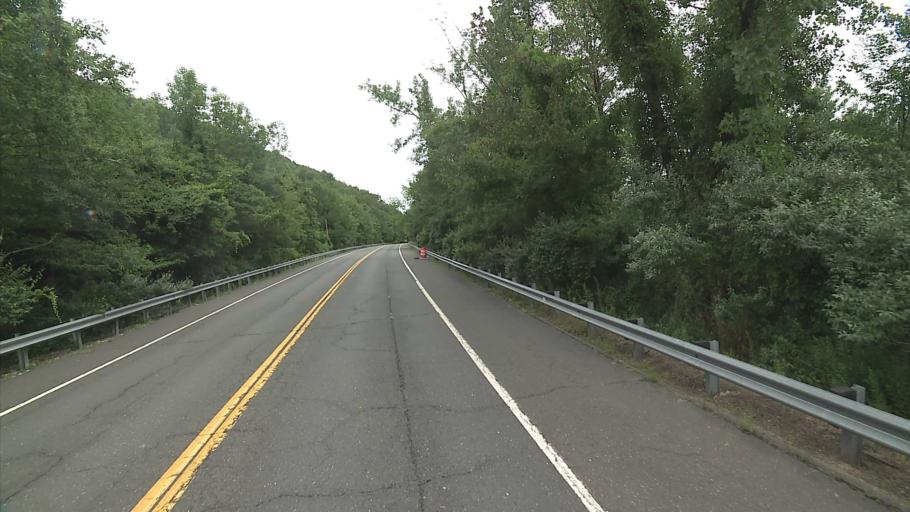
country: US
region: Connecticut
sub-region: Litchfield County
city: Winsted
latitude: 41.9986
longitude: -73.0471
